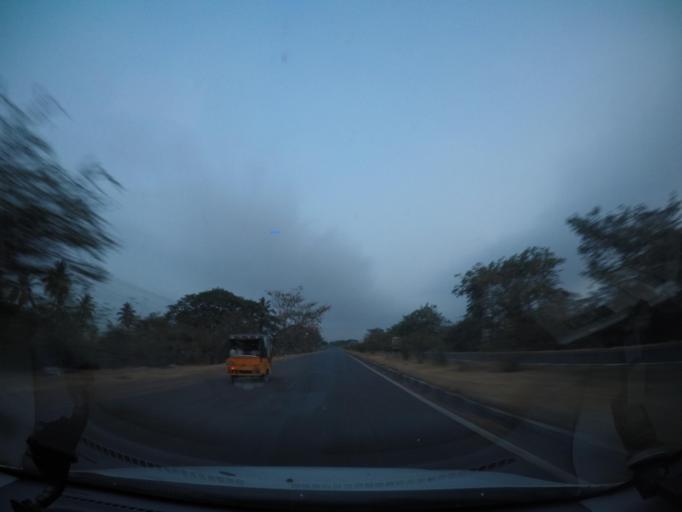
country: IN
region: Andhra Pradesh
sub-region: West Godavari
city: Tadepallegudem
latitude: 16.8186
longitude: 81.3948
